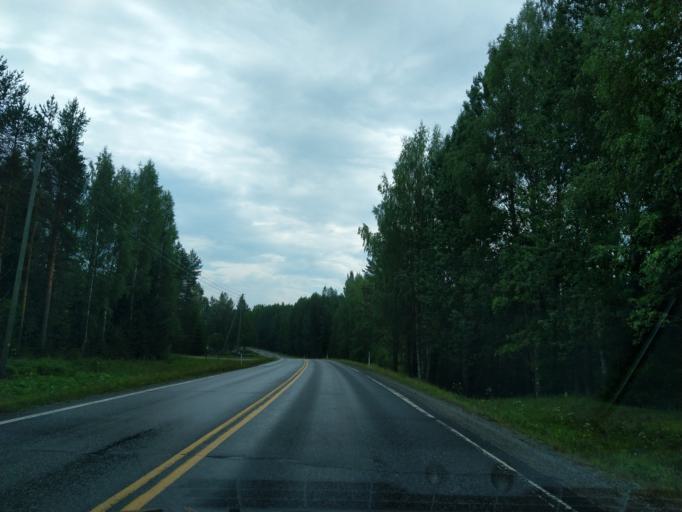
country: FI
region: Southern Savonia
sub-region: Savonlinna
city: Punkaharju
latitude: 61.6678
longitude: 29.4119
